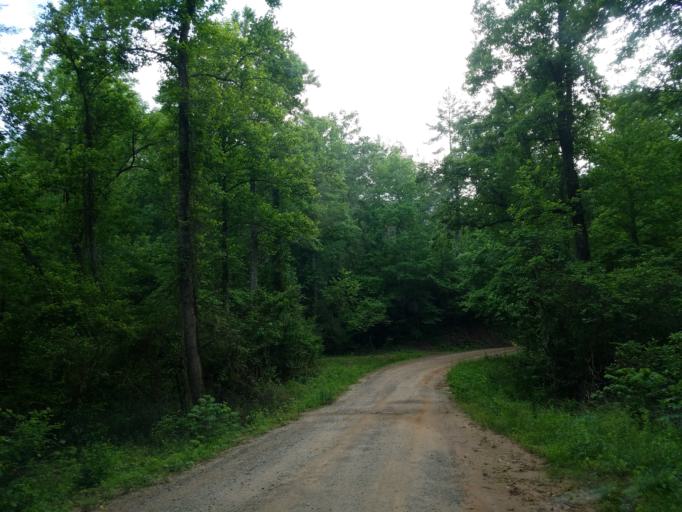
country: US
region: Georgia
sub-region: Lumpkin County
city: Dahlonega
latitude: 34.5982
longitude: -84.1129
